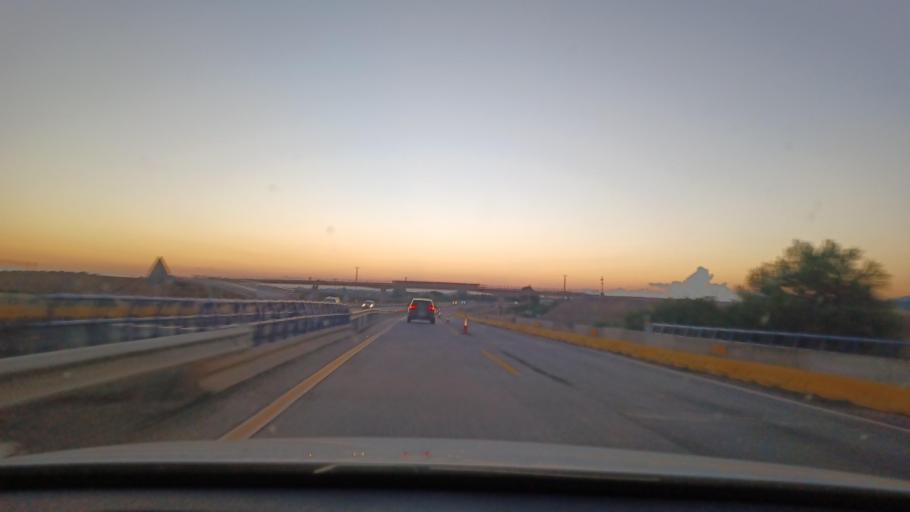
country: ES
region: Valencia
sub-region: Provincia de Valencia
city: Oliva
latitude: 38.9021
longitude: -0.1146
